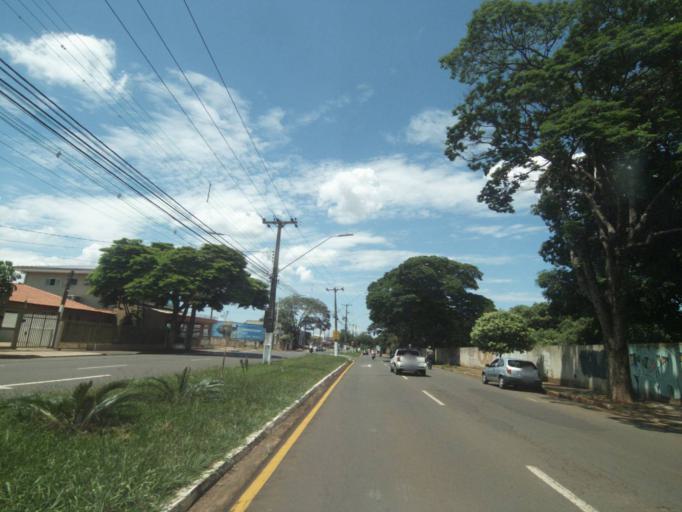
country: BR
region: Parana
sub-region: Londrina
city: Londrina
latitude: -23.3072
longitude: -51.2009
